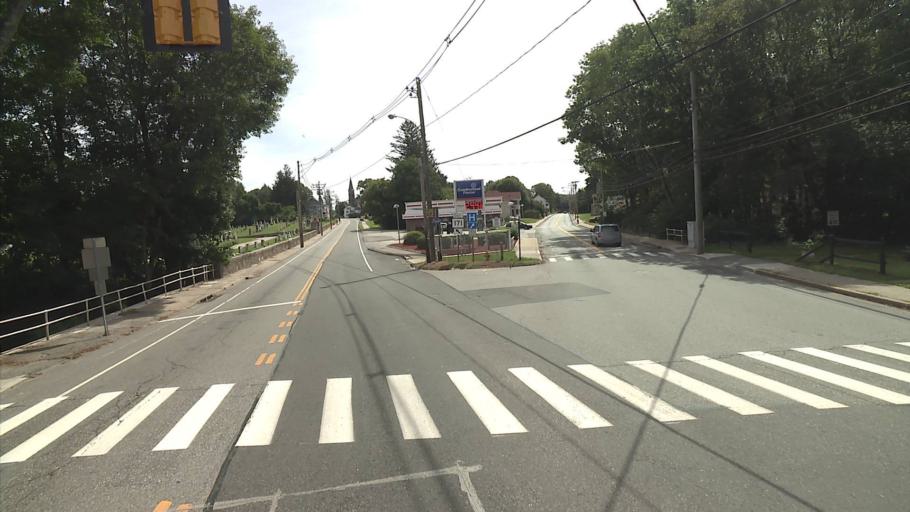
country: US
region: Connecticut
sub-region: Windham County
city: Putnam
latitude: 41.9242
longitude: -71.9175
